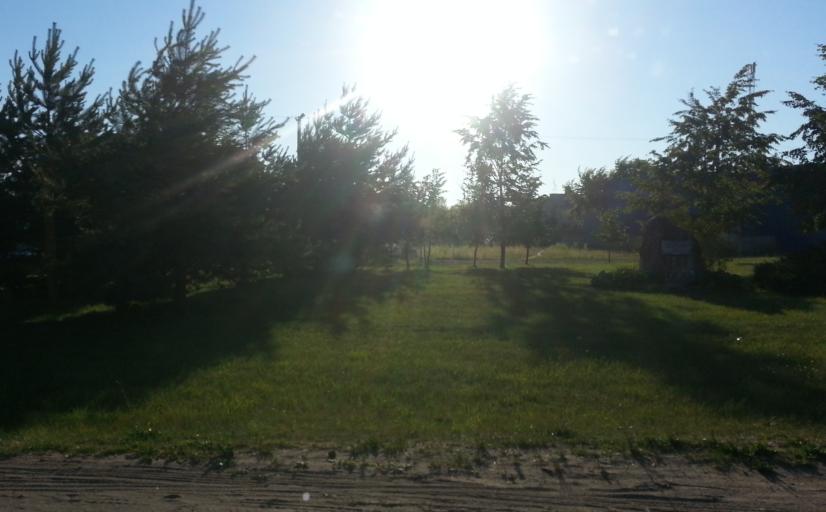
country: LT
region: Panevezys
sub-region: Panevezys City
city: Panevezys
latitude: 55.7801
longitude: 24.3640
